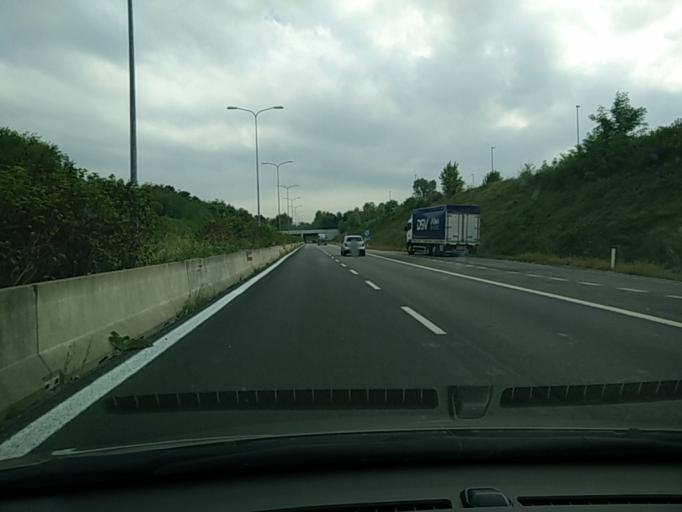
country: IT
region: Lombardy
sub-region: Provincia di Varese
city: Vizzola Ticino
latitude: 45.5951
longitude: 8.7140
